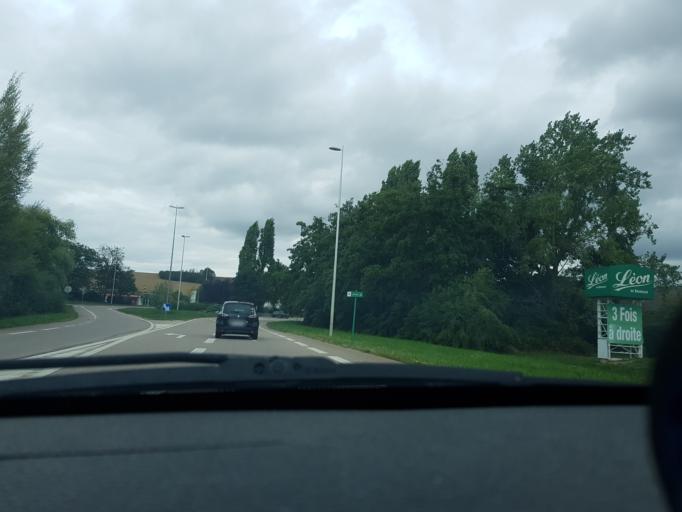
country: FR
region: Lorraine
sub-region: Departement de Meurthe-et-Moselle
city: Pulnoy
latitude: 48.7114
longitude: 6.2484
